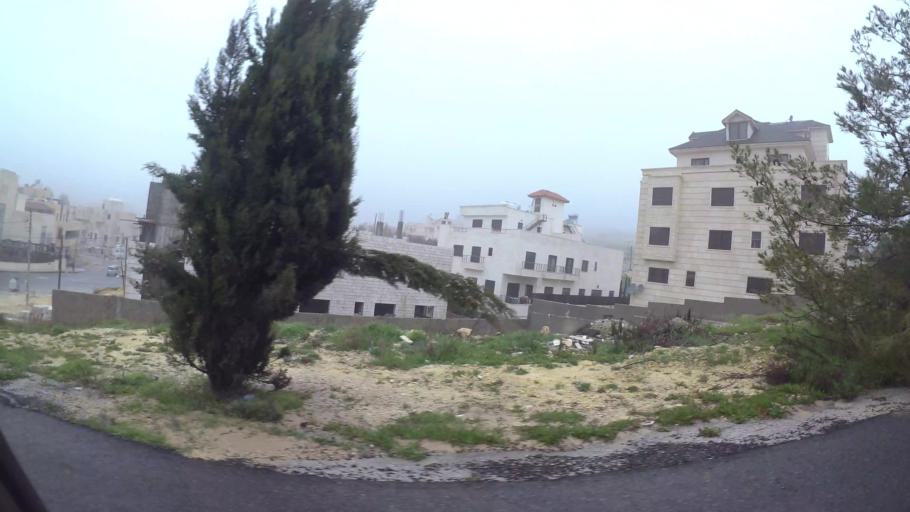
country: JO
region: Amman
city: Al Jubayhah
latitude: 32.0113
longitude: 35.8370
